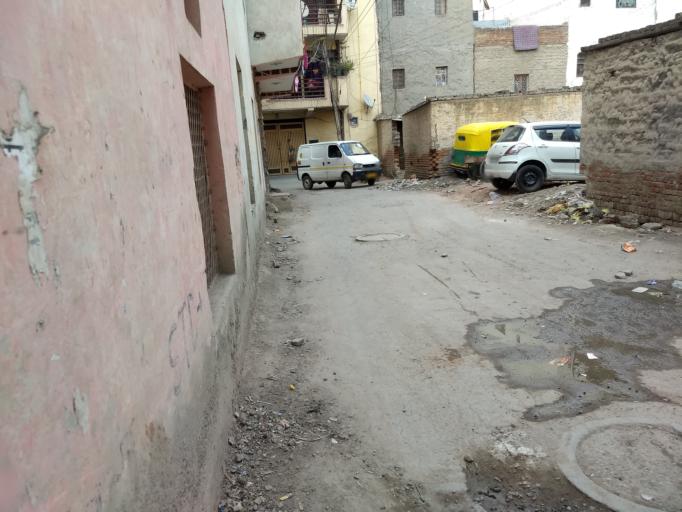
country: IN
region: NCT
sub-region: Central Delhi
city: Karol Bagh
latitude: 28.5411
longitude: 77.1253
